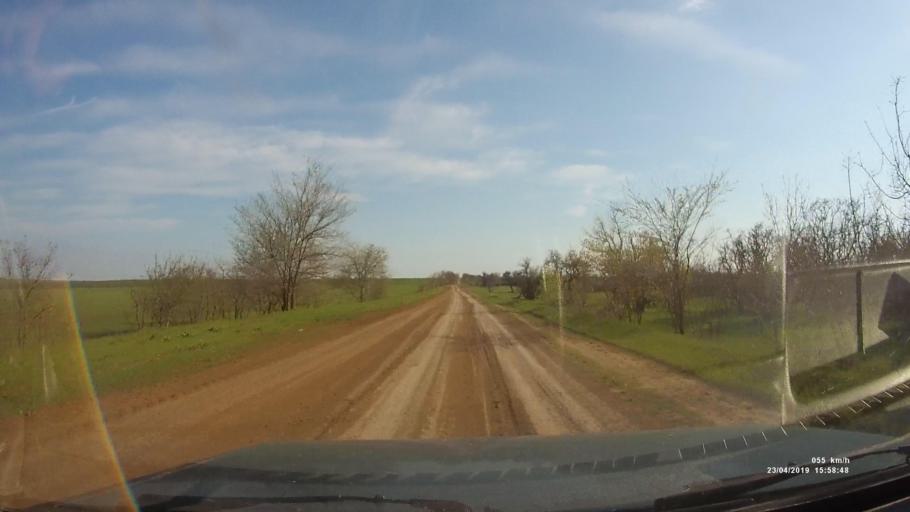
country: RU
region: Rostov
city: Remontnoye
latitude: 46.5212
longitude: 43.1095
